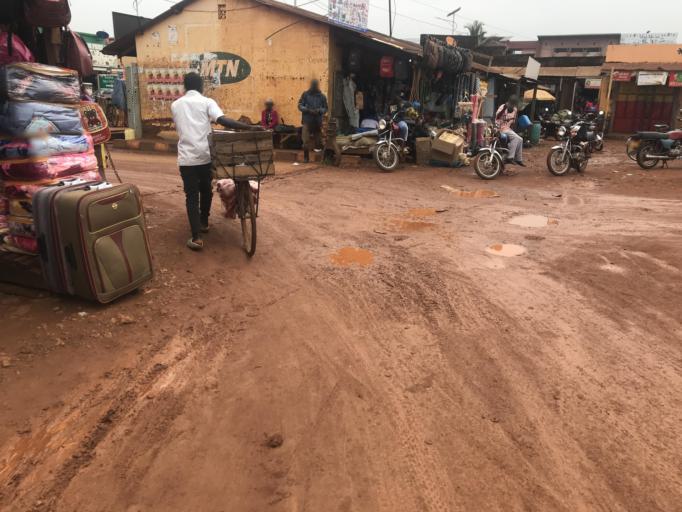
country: UG
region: Western Region
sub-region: Hoima District
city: Hoima
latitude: 1.4318
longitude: 31.3508
